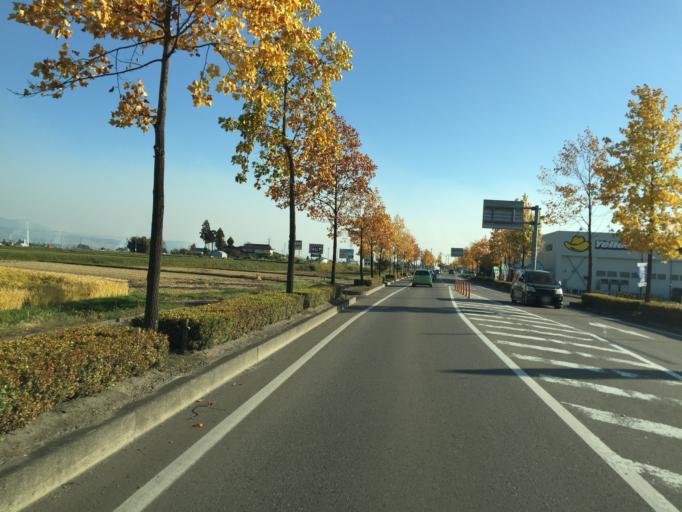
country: JP
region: Fukushima
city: Kitakata
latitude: 37.6481
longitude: 139.8883
